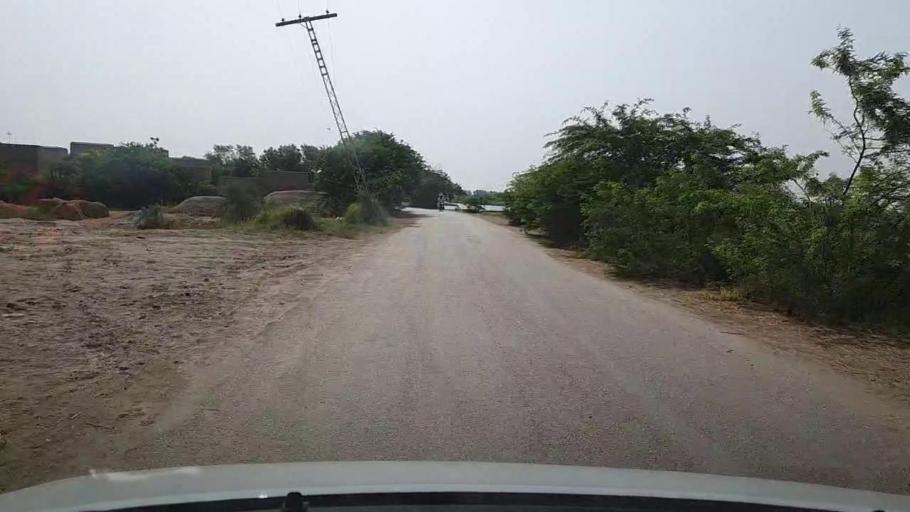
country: PK
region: Sindh
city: Mehar
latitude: 27.1211
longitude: 67.8490
